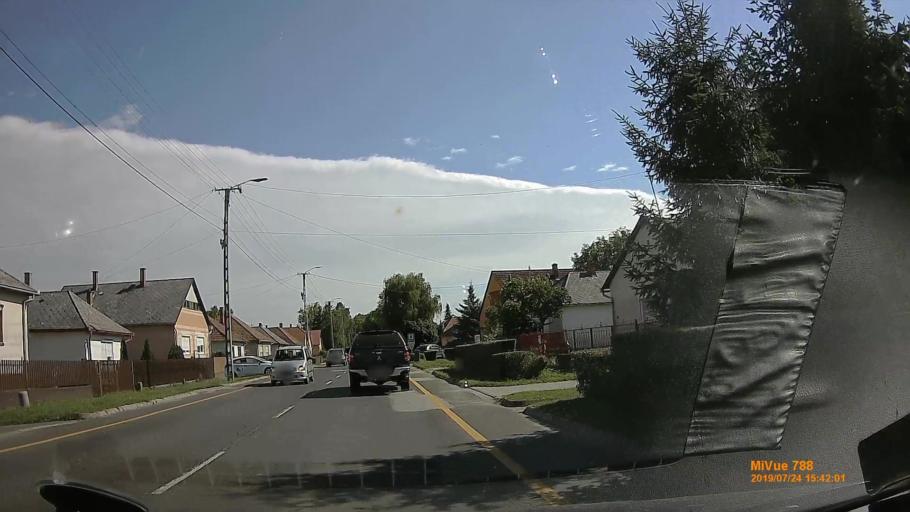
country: HU
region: Szabolcs-Szatmar-Bereg
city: Vasarosnameny
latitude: 48.1199
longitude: 22.3144
